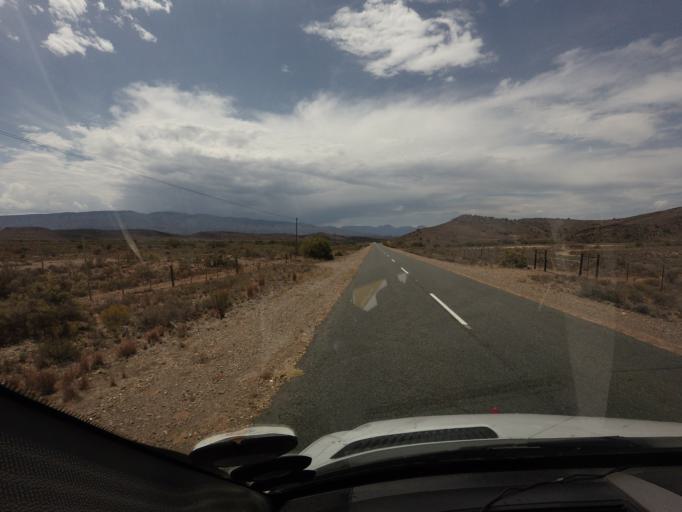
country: ZA
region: Western Cape
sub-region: Eden District Municipality
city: Ladismith
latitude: -33.6847
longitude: 20.9741
